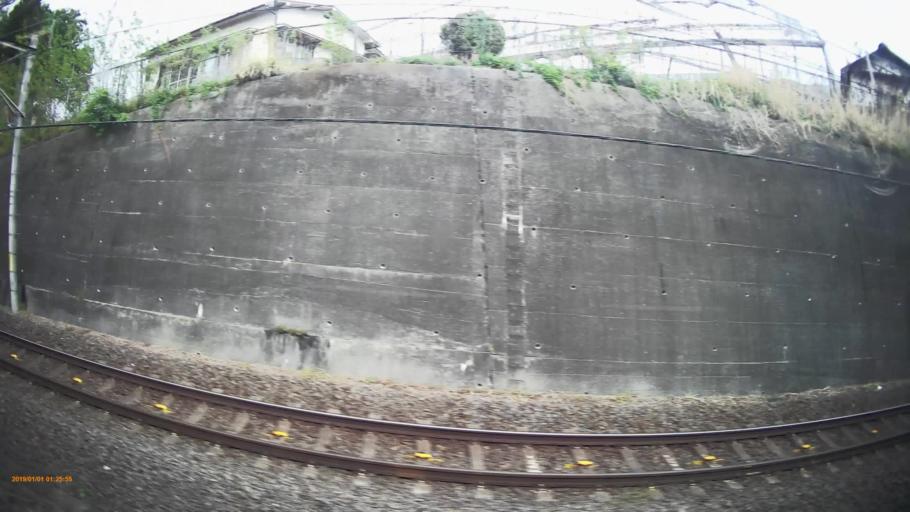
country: JP
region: Yamanashi
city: Enzan
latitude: 35.7024
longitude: 138.7430
